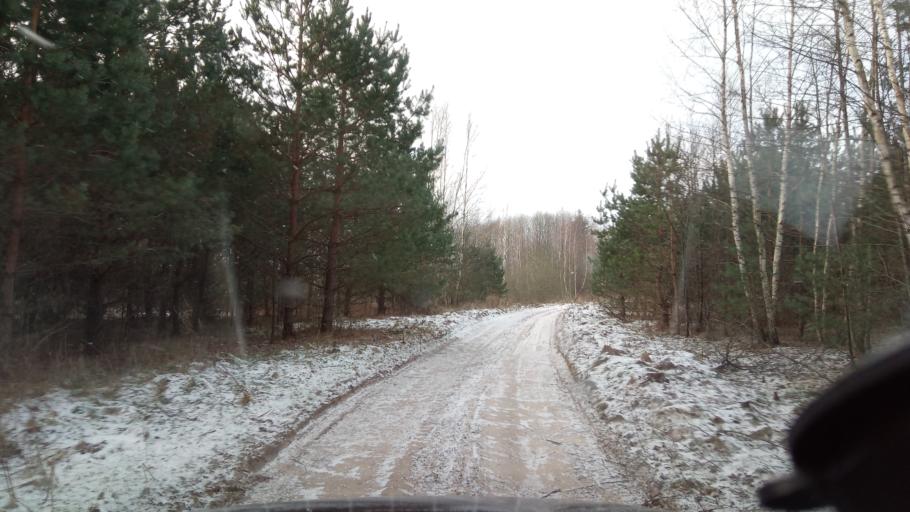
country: LT
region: Alytaus apskritis
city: Varena
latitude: 54.1257
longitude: 24.6747
